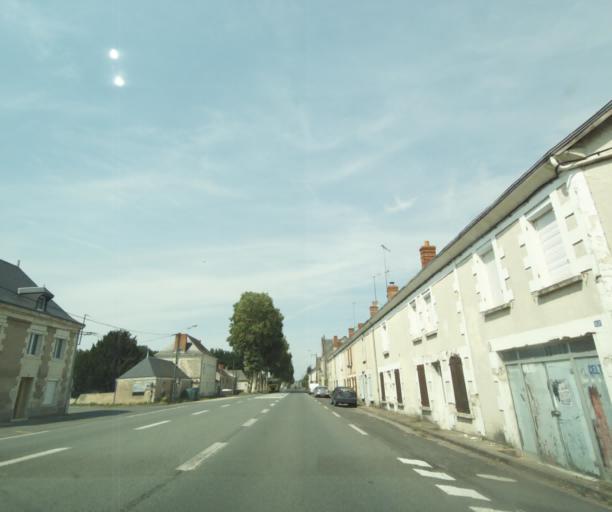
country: FR
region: Centre
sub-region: Departement d'Indre-et-Loire
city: La Celle-Saint-Avant
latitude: 47.0084
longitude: 0.6009
